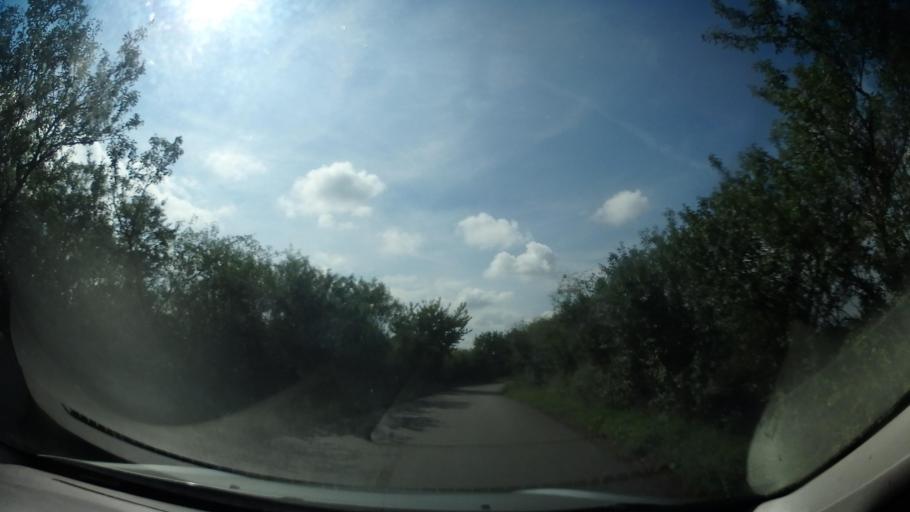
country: CZ
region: Central Bohemia
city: Krasna Hora nad Vltavou
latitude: 49.6797
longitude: 14.3211
